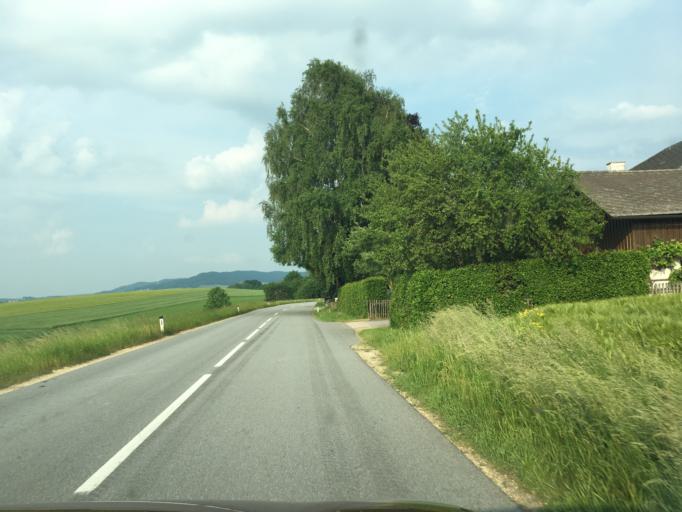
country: AT
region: Upper Austria
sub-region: Politischer Bezirk Ried im Innkreis
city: Ried im Innkreis
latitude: 48.1512
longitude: 13.5316
